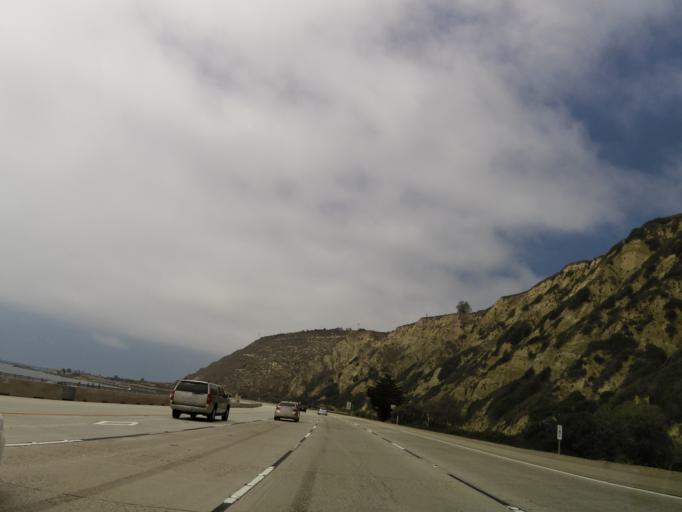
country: US
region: California
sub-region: Santa Barbara County
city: Carpinteria
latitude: 34.3533
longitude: -119.4276
